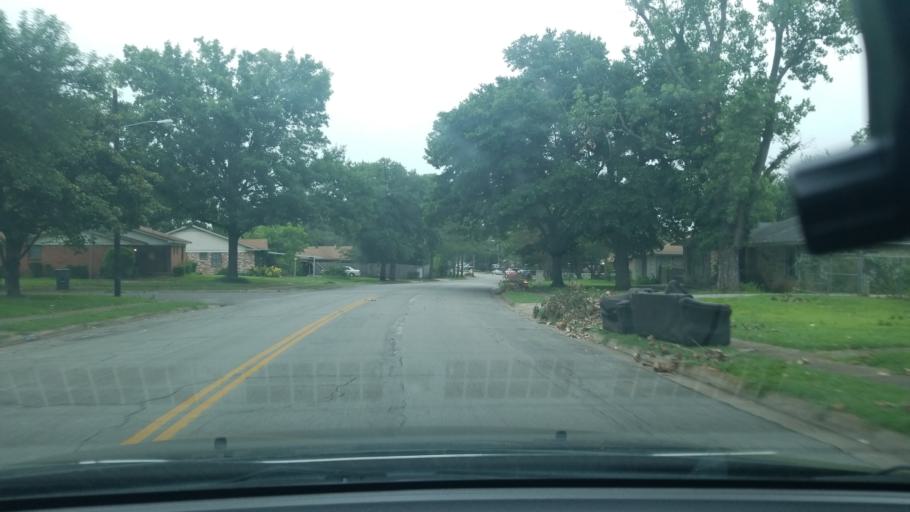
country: US
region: Texas
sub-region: Dallas County
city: Balch Springs
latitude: 32.7575
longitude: -96.6735
